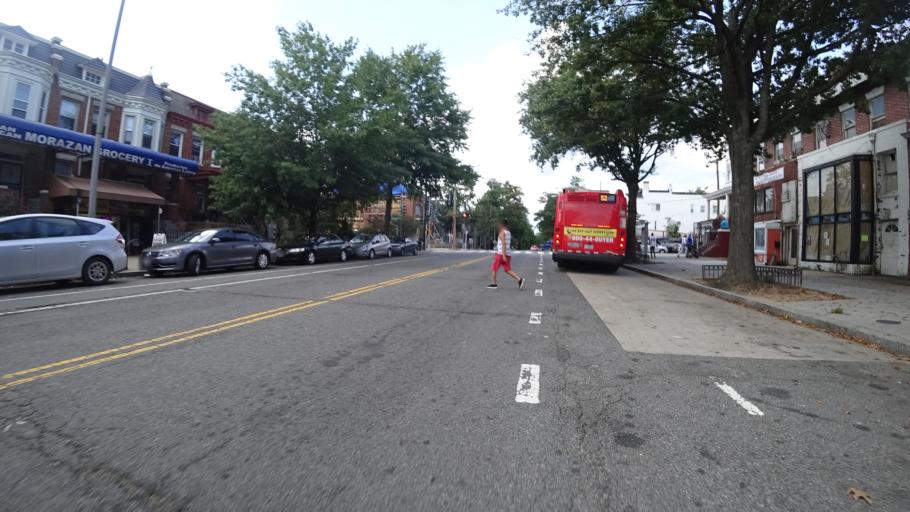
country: US
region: Washington, D.C.
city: Washington, D.C.
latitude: 38.9393
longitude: -77.0327
